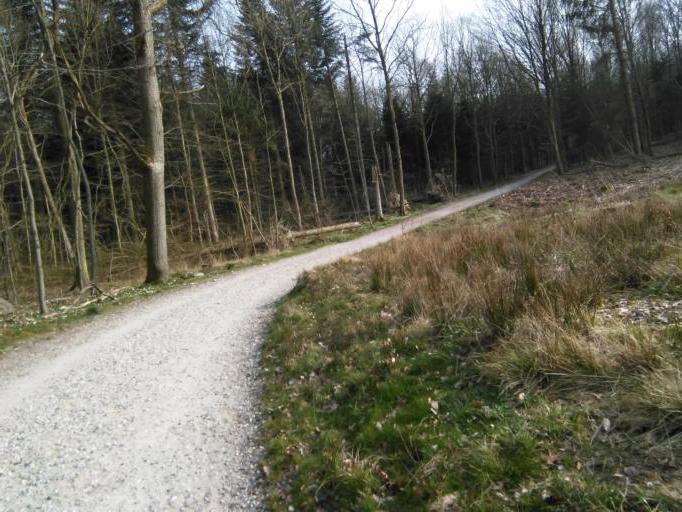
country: DK
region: Central Jutland
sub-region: Arhus Kommune
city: Beder
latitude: 56.0797
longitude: 10.2466
